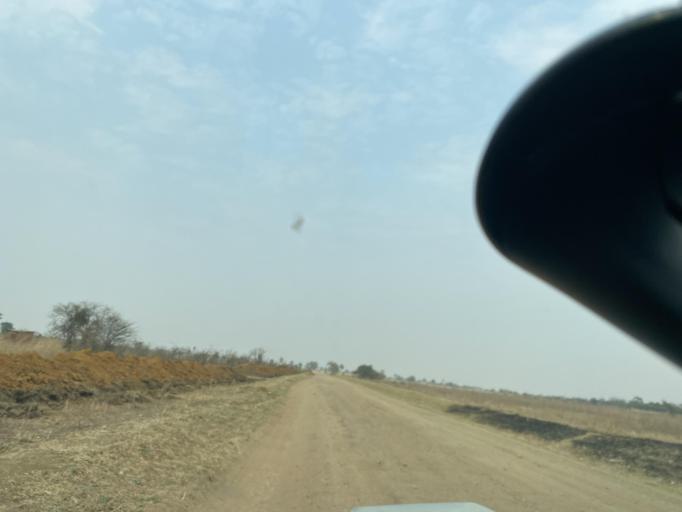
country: ZM
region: Lusaka
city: Kafue
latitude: -15.6446
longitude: 28.0835
